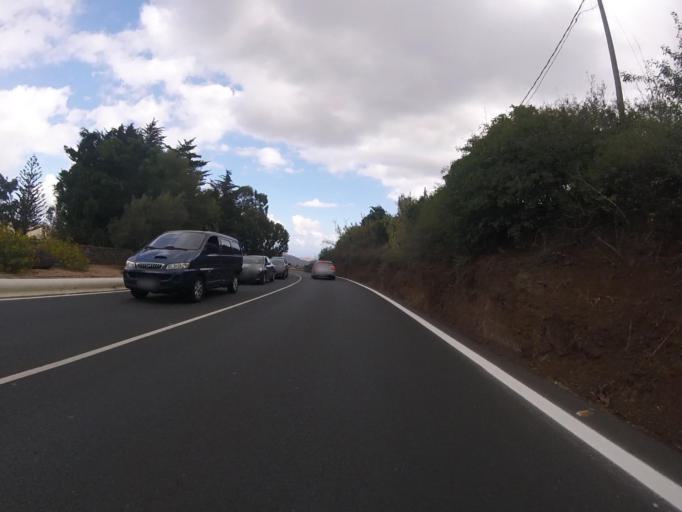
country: ES
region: Canary Islands
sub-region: Provincia de Las Palmas
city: Vega de San Mateo
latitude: 28.0162
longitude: -15.5242
